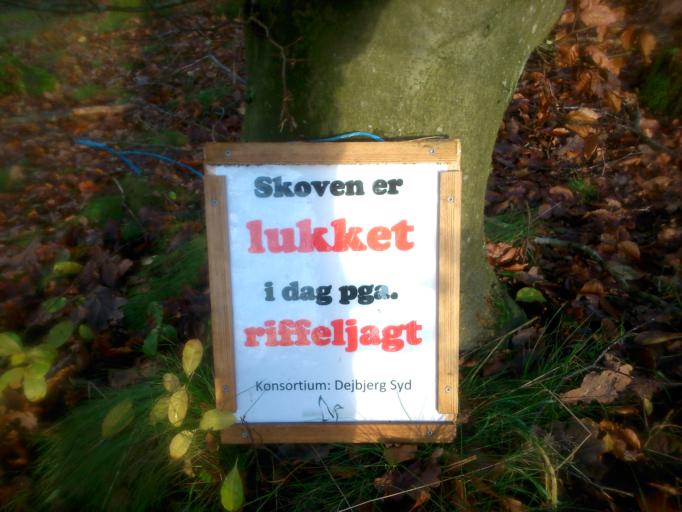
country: DK
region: Central Jutland
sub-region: Ringkobing-Skjern Kommune
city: Skjern
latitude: 55.9967
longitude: 8.4612
